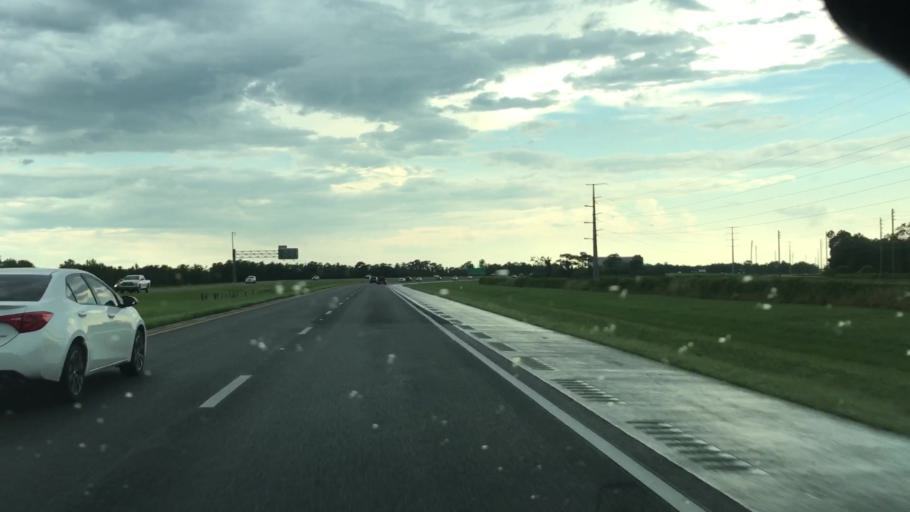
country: US
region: Florida
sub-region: Orange County
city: Meadow Woods
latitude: 28.3883
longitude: -81.2574
